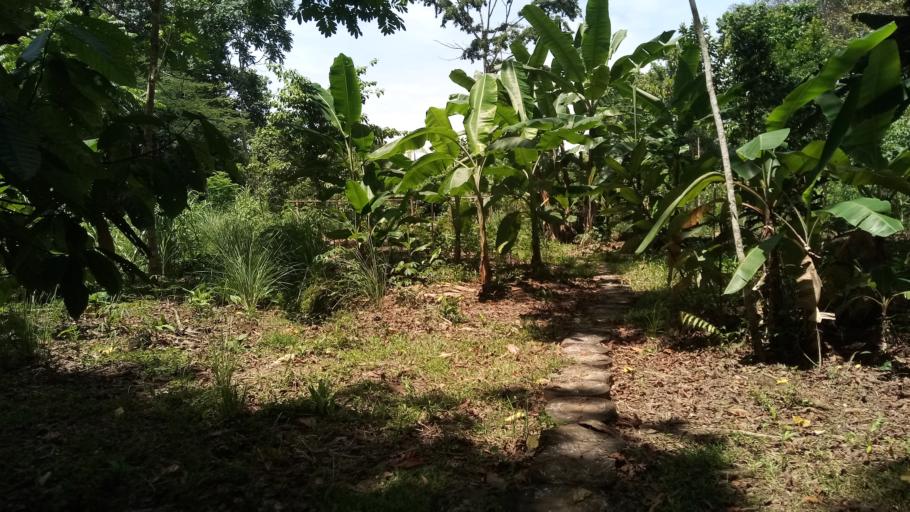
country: CR
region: Limon
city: Sixaola
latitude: 9.6242
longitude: -82.6213
